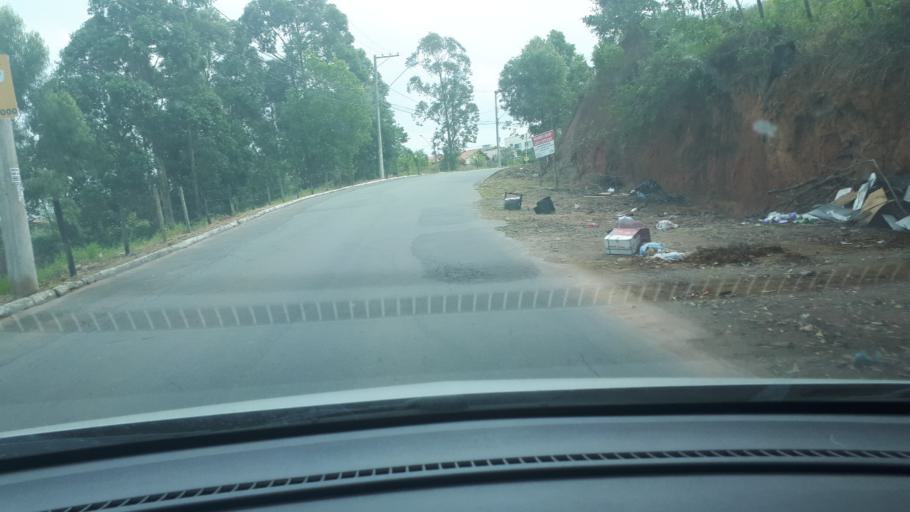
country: BR
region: Espirito Santo
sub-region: Serra
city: Serra
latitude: -20.1482
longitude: -40.1930
